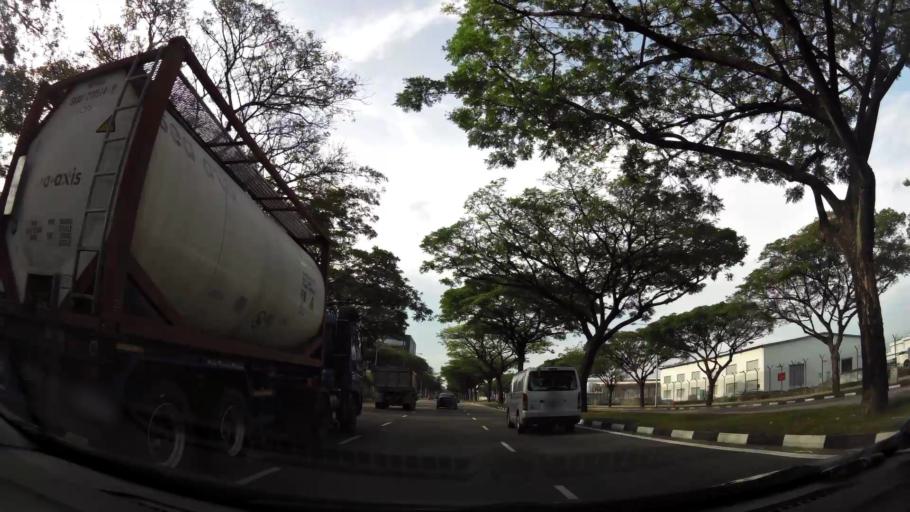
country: MY
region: Johor
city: Johor Bahru
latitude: 1.3066
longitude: 103.6260
